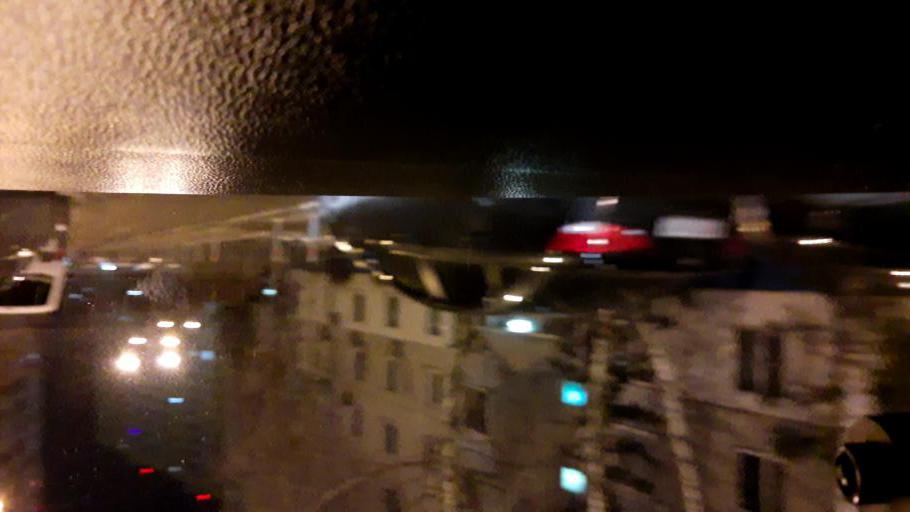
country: RU
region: Moskovskaya
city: Vidnoye
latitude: 55.5435
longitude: 37.7149
